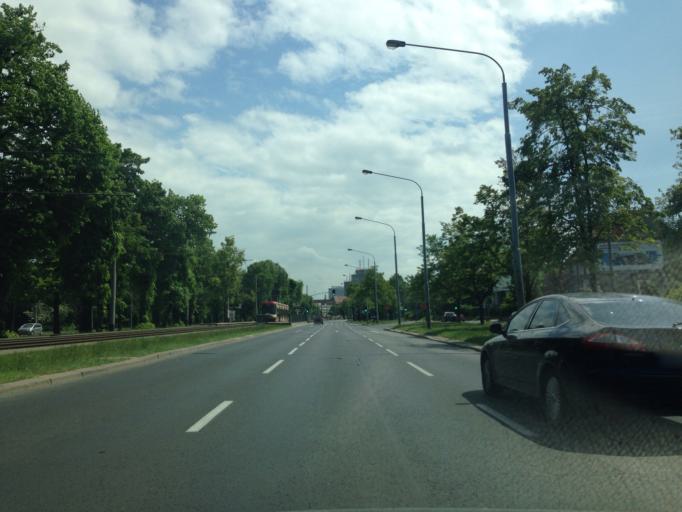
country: PL
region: Pomeranian Voivodeship
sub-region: Gdansk
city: Gdansk
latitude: 54.3645
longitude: 18.6373
